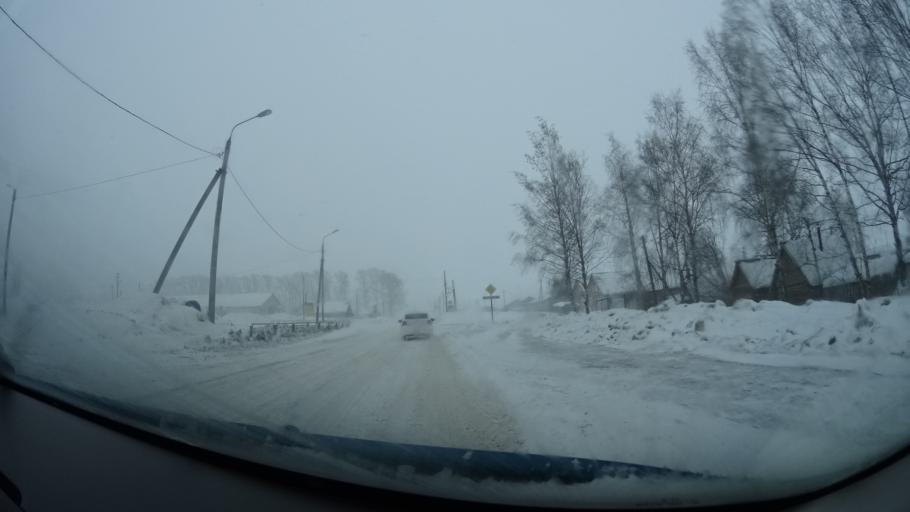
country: RU
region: Perm
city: Kuyeda
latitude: 56.4231
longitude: 55.5832
